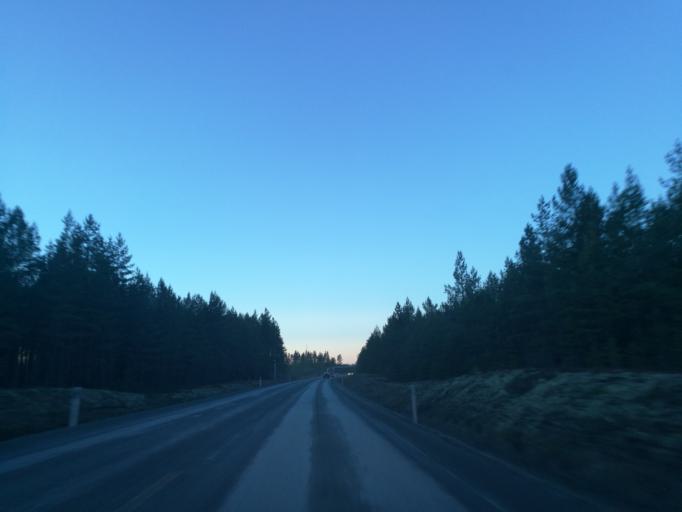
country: NO
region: Hedmark
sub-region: Eidskog
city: Skotterud
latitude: 59.9442
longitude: 12.1801
